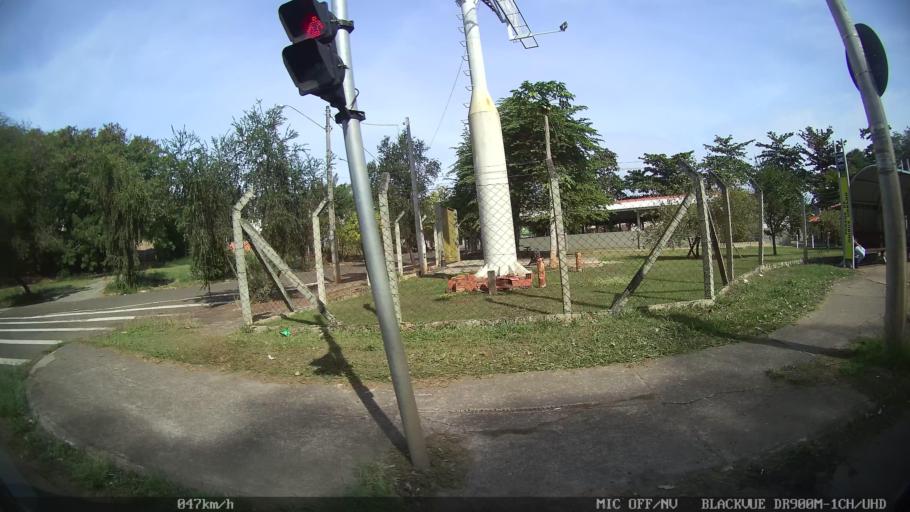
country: BR
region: Sao Paulo
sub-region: Piracicaba
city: Piracicaba
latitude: -22.7261
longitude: -47.6691
